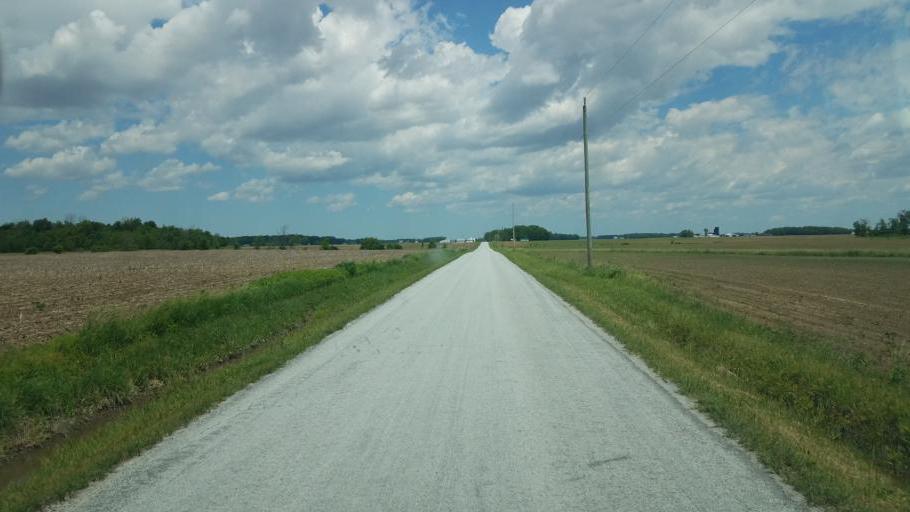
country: US
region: Ohio
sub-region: Hardin County
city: Kenton
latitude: 40.6588
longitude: -83.4775
